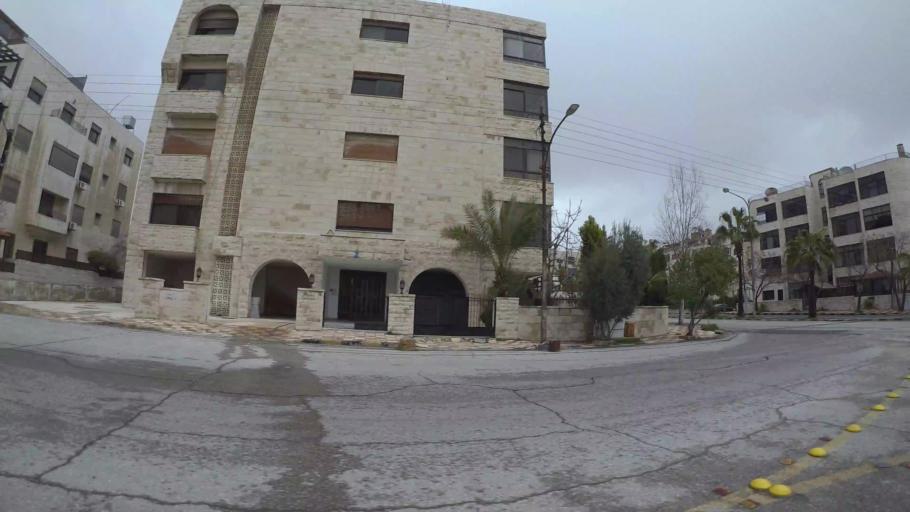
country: JO
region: Amman
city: Wadi as Sir
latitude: 31.9485
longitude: 35.8699
